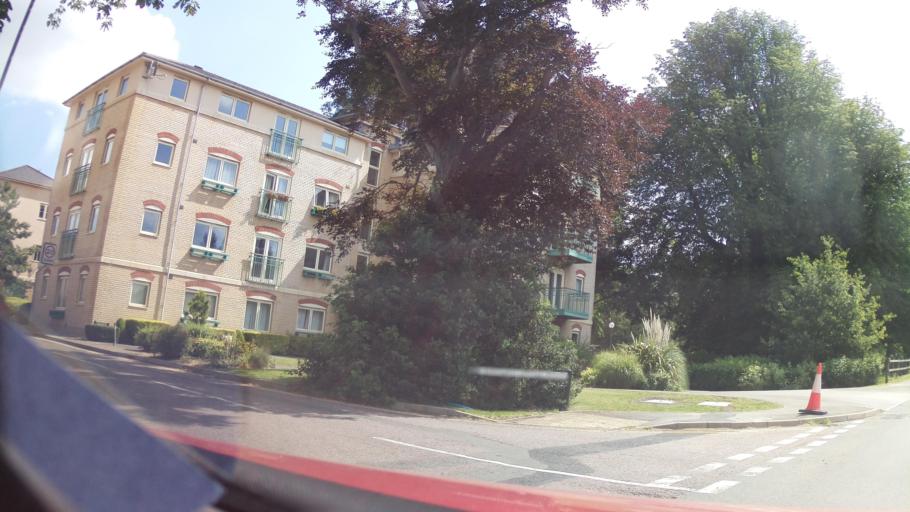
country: GB
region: England
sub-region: Wiltshire
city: Malmesbury
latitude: 51.5760
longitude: -2.0842
